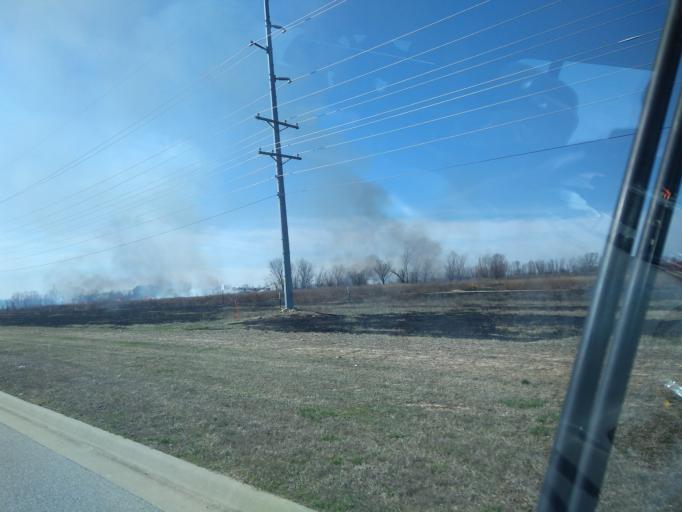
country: US
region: Arkansas
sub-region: Washington County
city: Farmington
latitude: 36.0687
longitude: -94.2310
